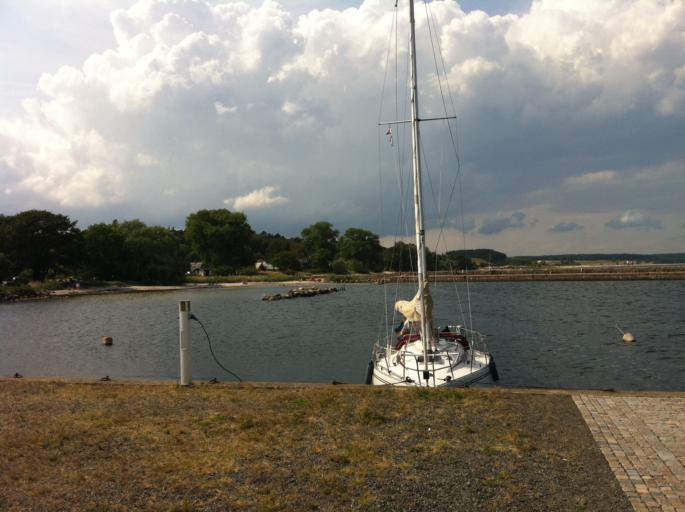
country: SE
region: Skane
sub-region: Simrishamns Kommun
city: Kivik
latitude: 55.6880
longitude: 14.2274
